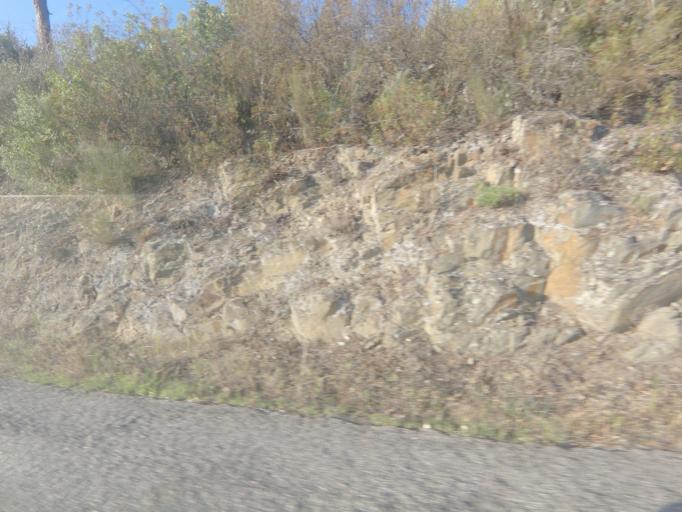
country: PT
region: Viseu
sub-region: Armamar
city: Armamar
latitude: 41.1308
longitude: -7.6773
